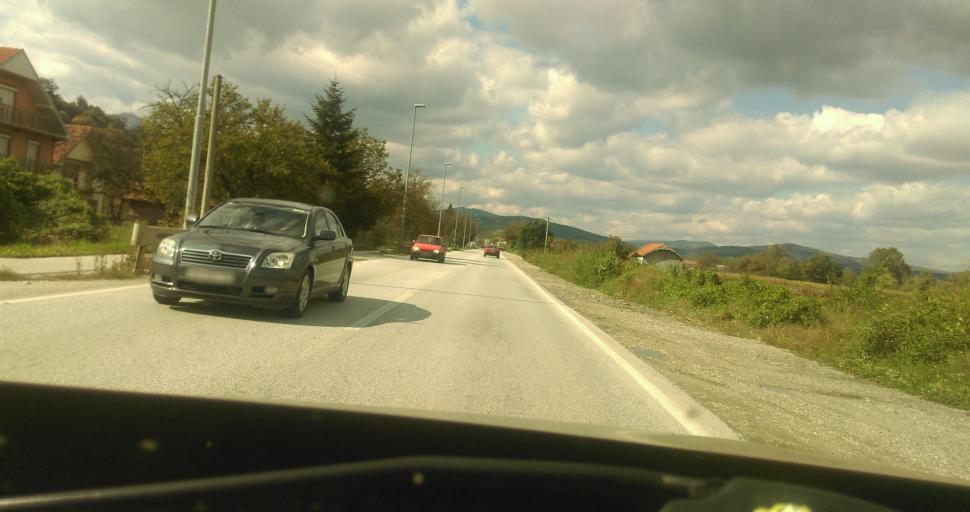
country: RS
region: Central Serbia
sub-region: Moravicki Okrug
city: Cacak
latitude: 43.8940
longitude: 20.3018
